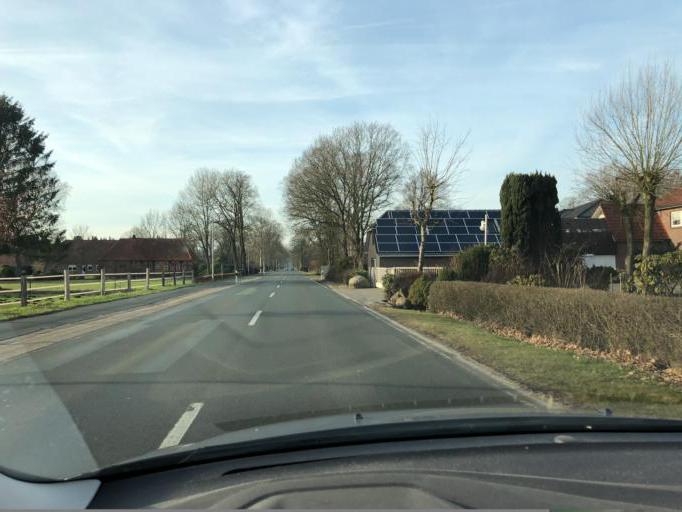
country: DE
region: Lower Saxony
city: Bad Zwischenahn
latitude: 53.1429
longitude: 8.1000
